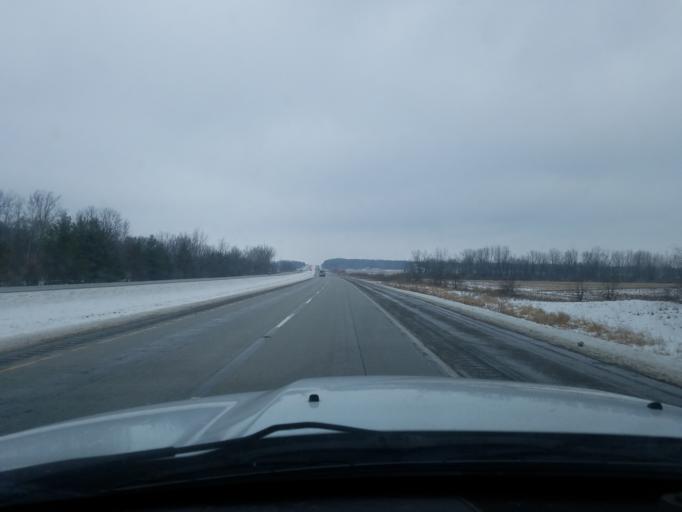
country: US
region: Indiana
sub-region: Fulton County
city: Rochester
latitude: 41.0973
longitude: -86.2398
